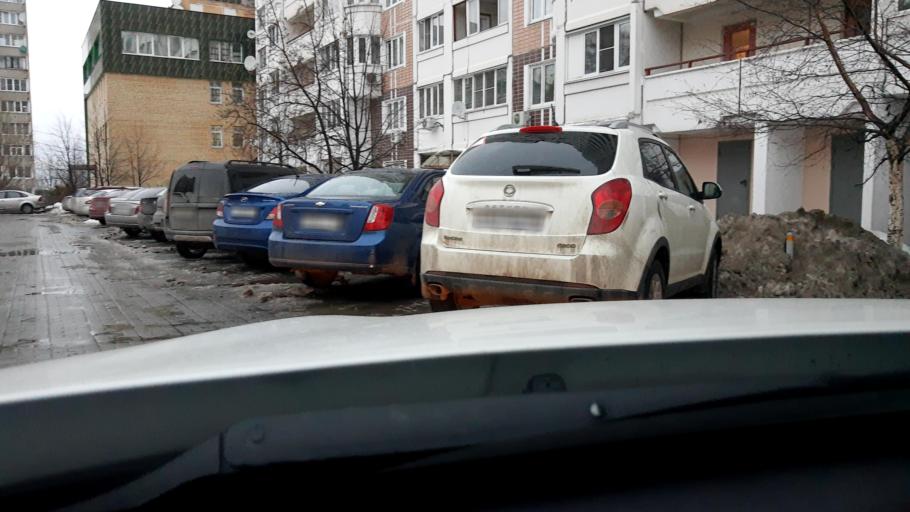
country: RU
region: Moskovskaya
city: Domodedovo
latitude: 55.4530
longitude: 37.7459
